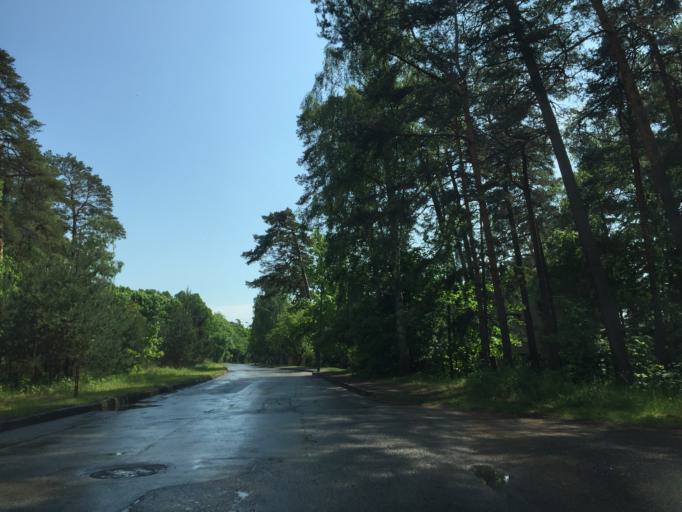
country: LT
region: Klaipedos apskritis
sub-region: Klaipeda
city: Klaipeda
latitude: 55.7700
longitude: 21.0841
